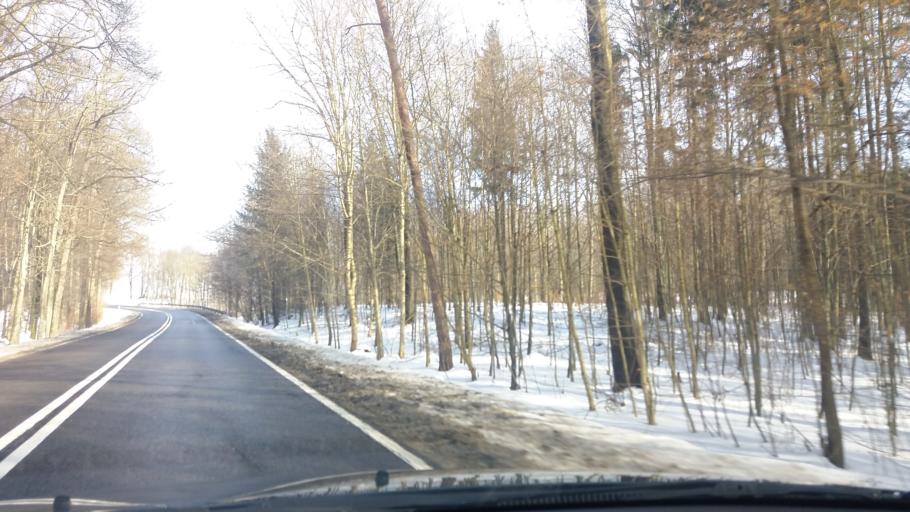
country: PL
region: Warmian-Masurian Voivodeship
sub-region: Powiat olsztynski
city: Czerwonka
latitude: 53.9540
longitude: 20.9068
